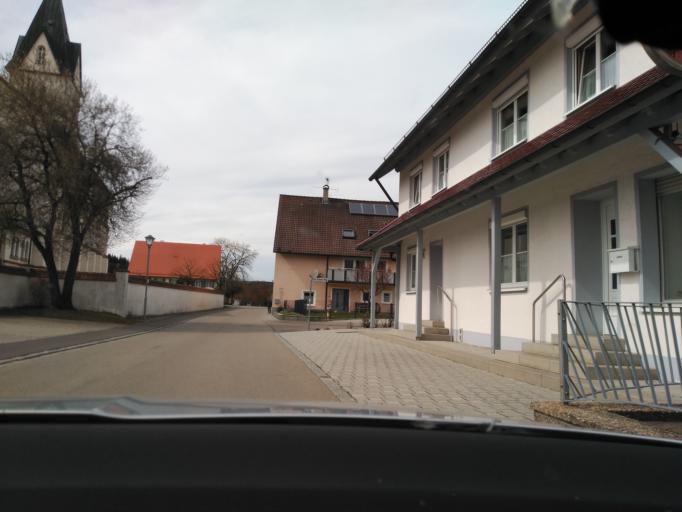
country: DE
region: Baden-Wuerttemberg
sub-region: Tuebingen Region
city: Aichstetten
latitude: 47.8956
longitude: 10.0806
